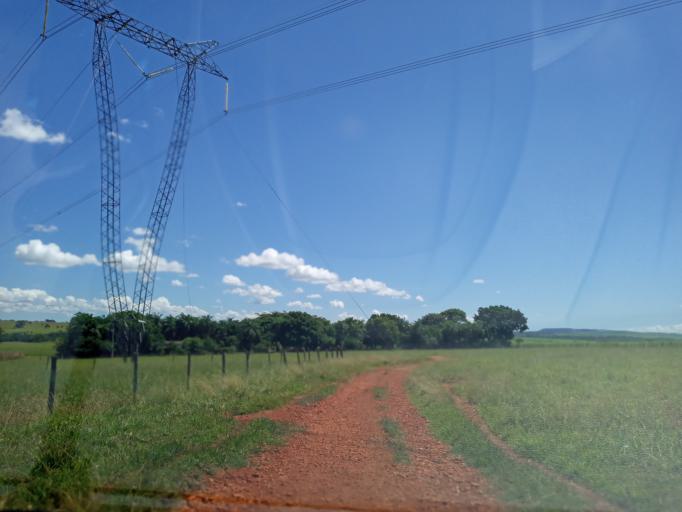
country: BR
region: Goias
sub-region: Itumbiara
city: Itumbiara
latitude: -18.3957
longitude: -49.1248
